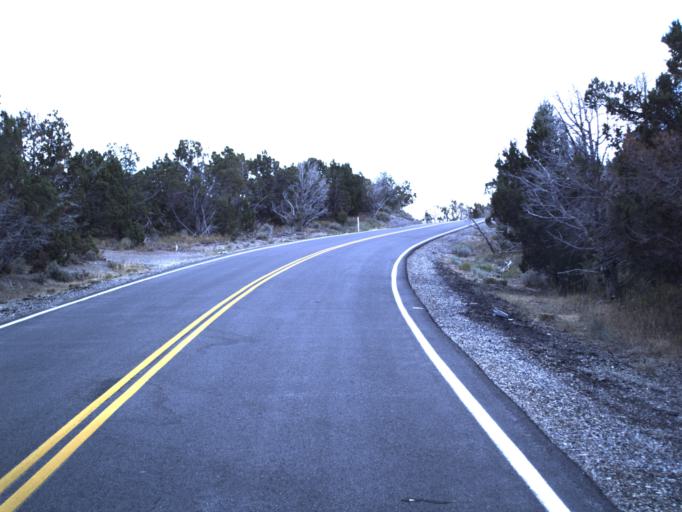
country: US
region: Utah
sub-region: Tooele County
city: Grantsville
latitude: 40.3383
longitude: -112.5734
